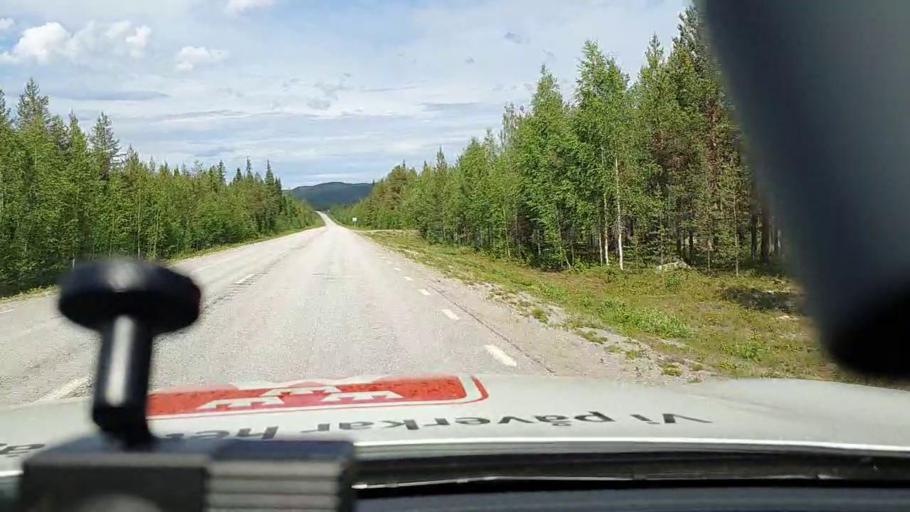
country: SE
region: Norrbotten
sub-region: Jokkmokks Kommun
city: Jokkmokk
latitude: 66.5446
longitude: 20.1367
